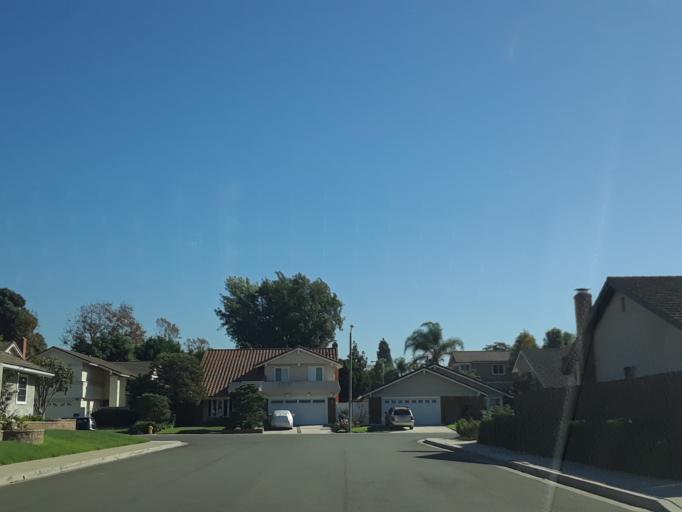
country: US
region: California
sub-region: Orange County
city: Tustin
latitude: 33.7103
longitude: -117.7860
